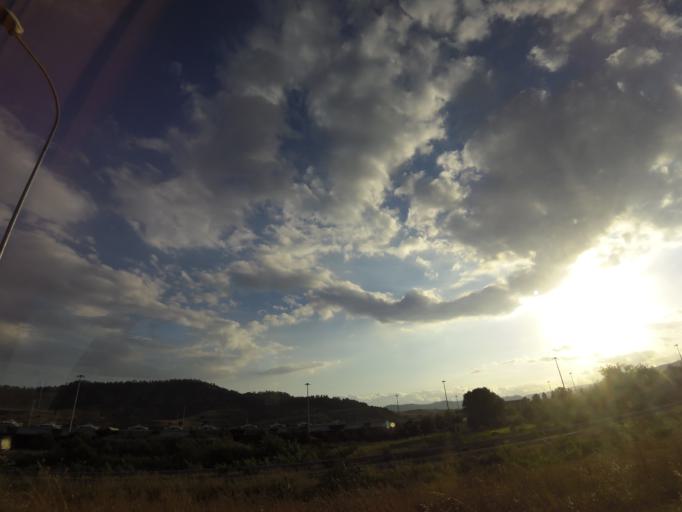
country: IT
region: Calabria
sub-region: Provincia di Catanzaro
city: Catanzaro
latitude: 38.8566
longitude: 16.5732
